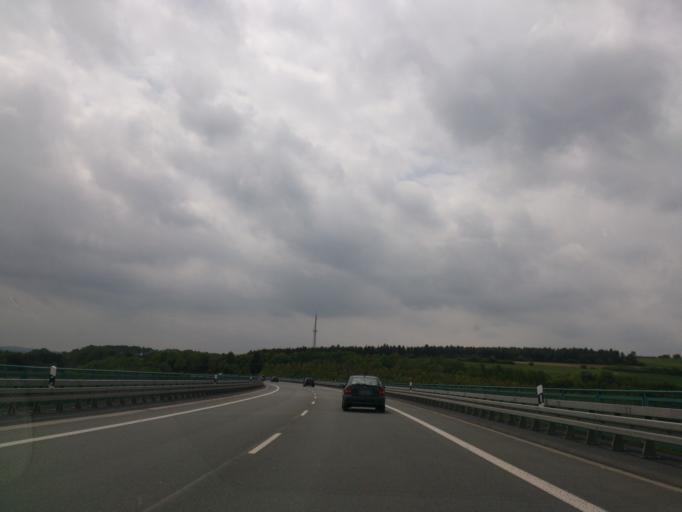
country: DE
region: North Rhine-Westphalia
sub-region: Regierungsbezirk Detmold
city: Willebadessen
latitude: 51.5379
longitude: 9.0218
